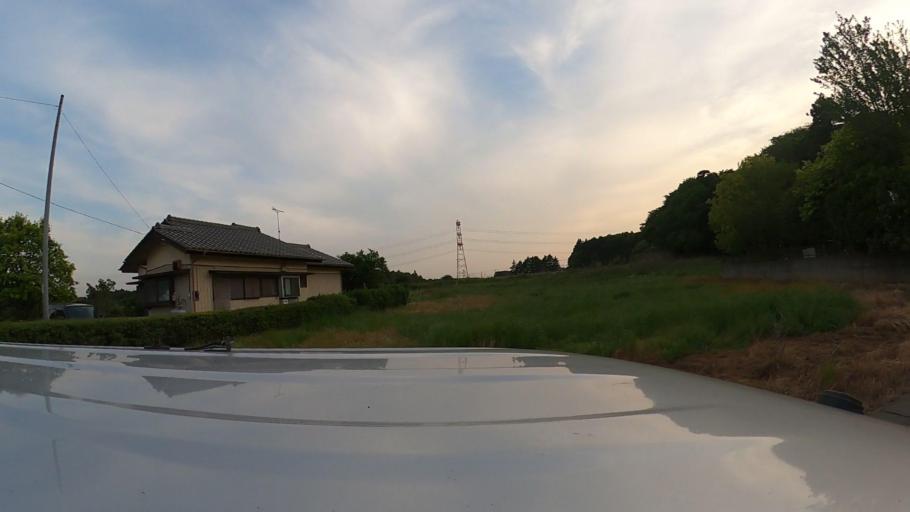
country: JP
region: Ibaraki
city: Ushiku
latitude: 36.0107
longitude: 140.1075
